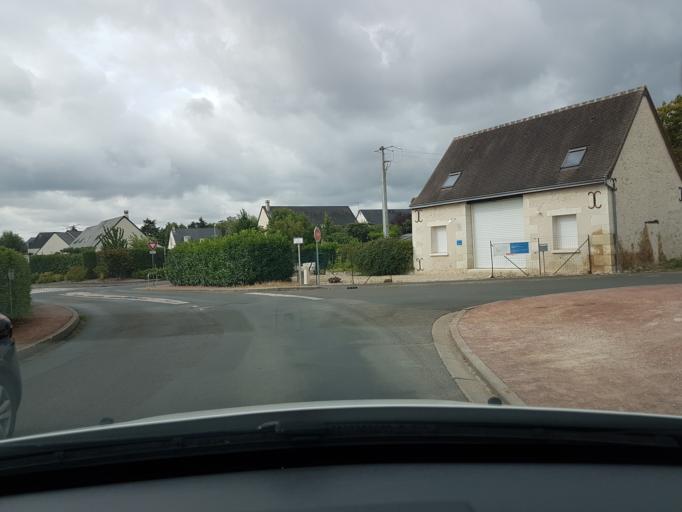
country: FR
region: Centre
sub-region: Departement d'Indre-et-Loire
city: Larcay
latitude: 47.3615
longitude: 0.7744
